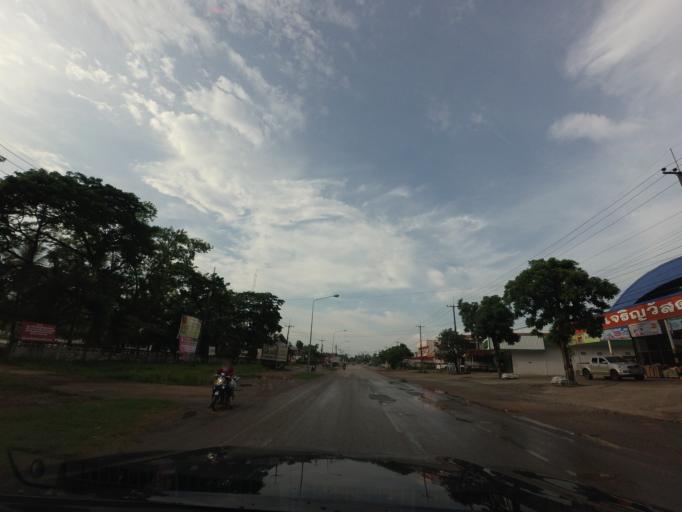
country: TH
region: Nong Khai
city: Pho Tak
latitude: 17.7750
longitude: 102.3955
